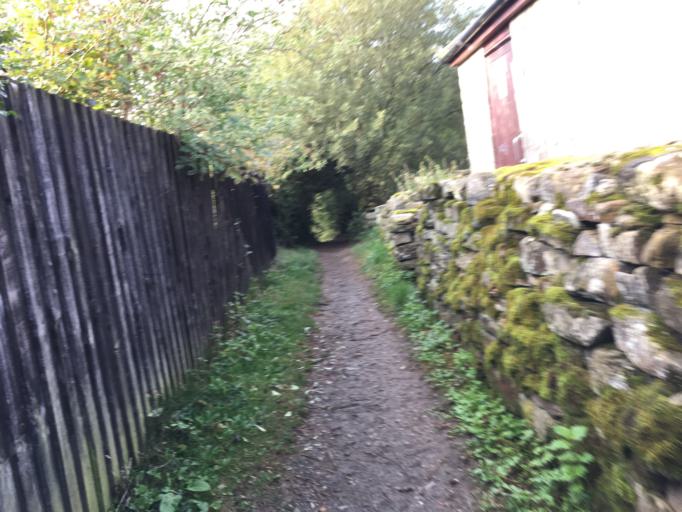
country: GB
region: England
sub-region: North Yorkshire
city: Sleights
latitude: 54.3959
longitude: -0.7272
